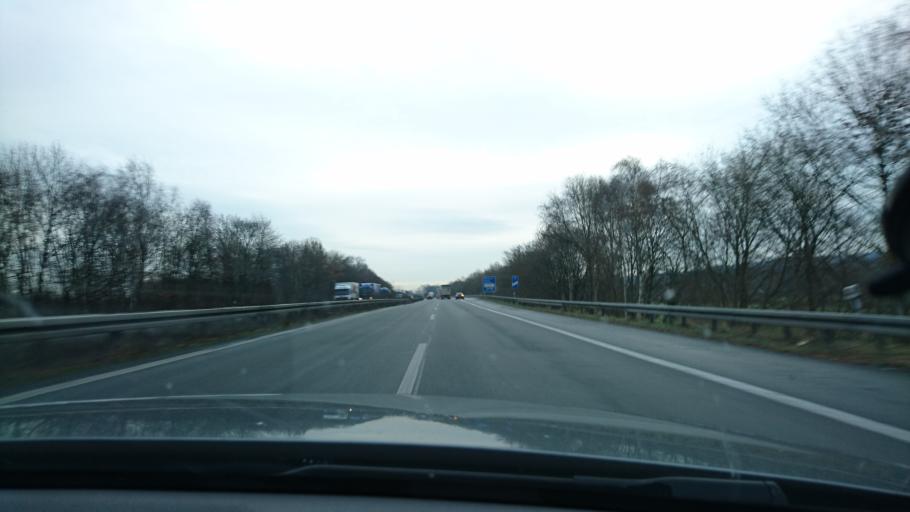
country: DE
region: North Rhine-Westphalia
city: Ibbenburen
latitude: 52.2591
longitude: 7.7016
